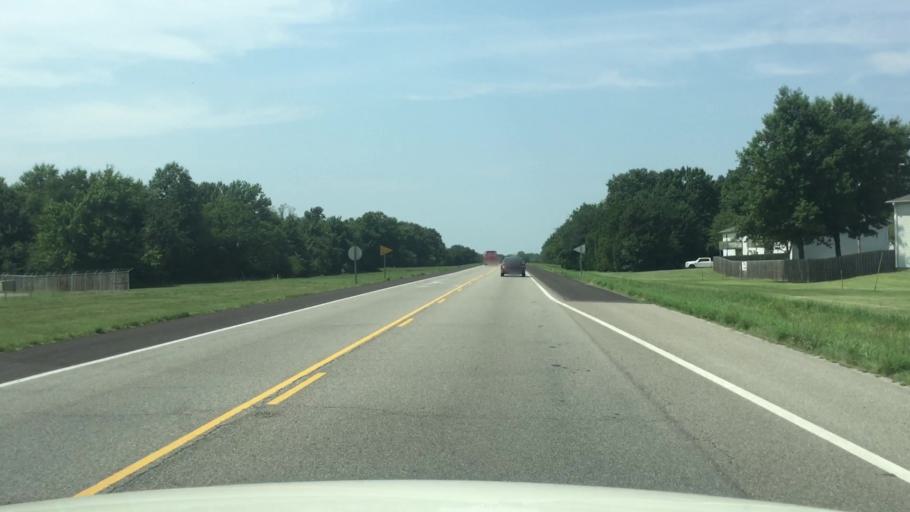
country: US
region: Kansas
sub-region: Crawford County
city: Pittsburg
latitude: 37.3877
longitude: -94.7115
